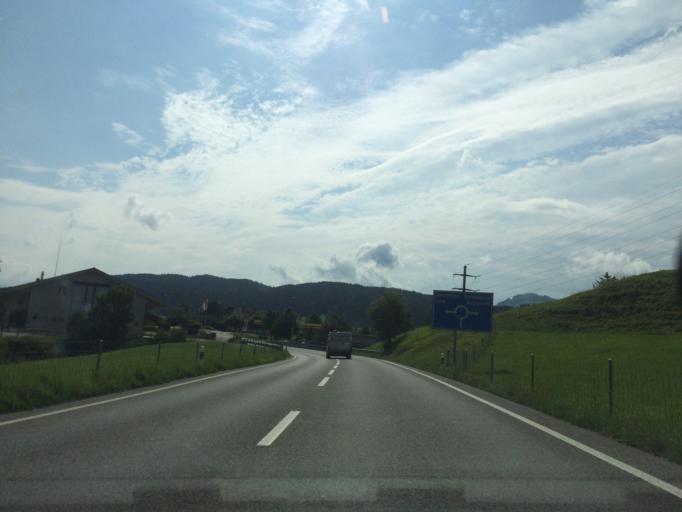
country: CH
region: Appenzell Ausserrhoden
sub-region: Bezirk Mittelland
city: Gais
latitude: 47.3596
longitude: 9.4420
